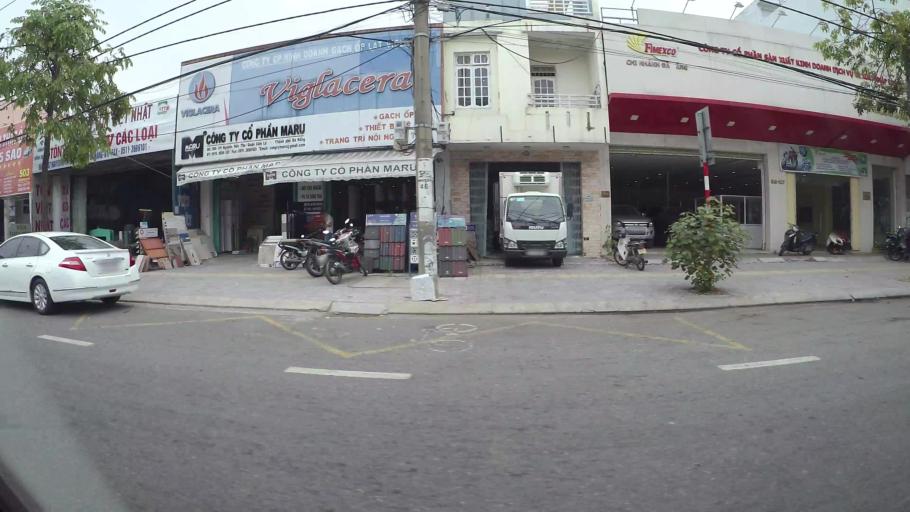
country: VN
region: Da Nang
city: Cam Le
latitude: 16.0330
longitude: 108.2092
